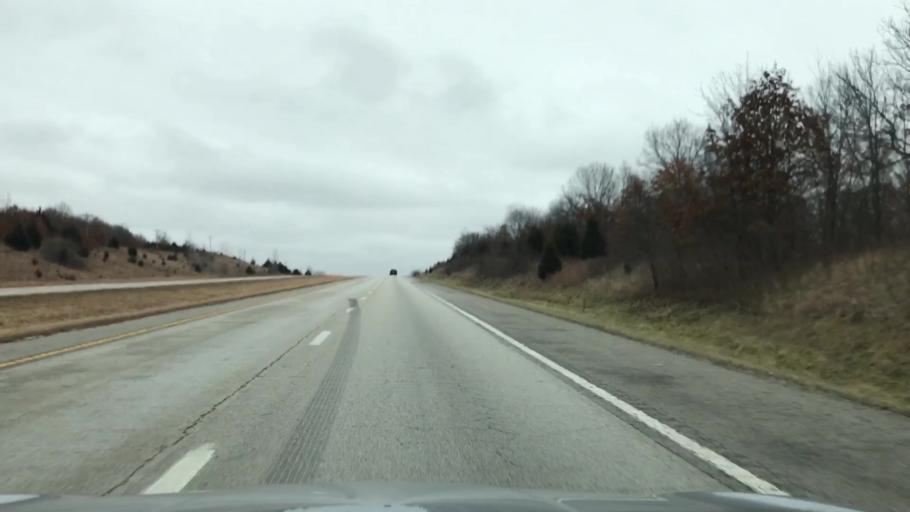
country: US
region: Missouri
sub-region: Clinton County
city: Cameron
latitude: 39.7512
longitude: -94.1553
